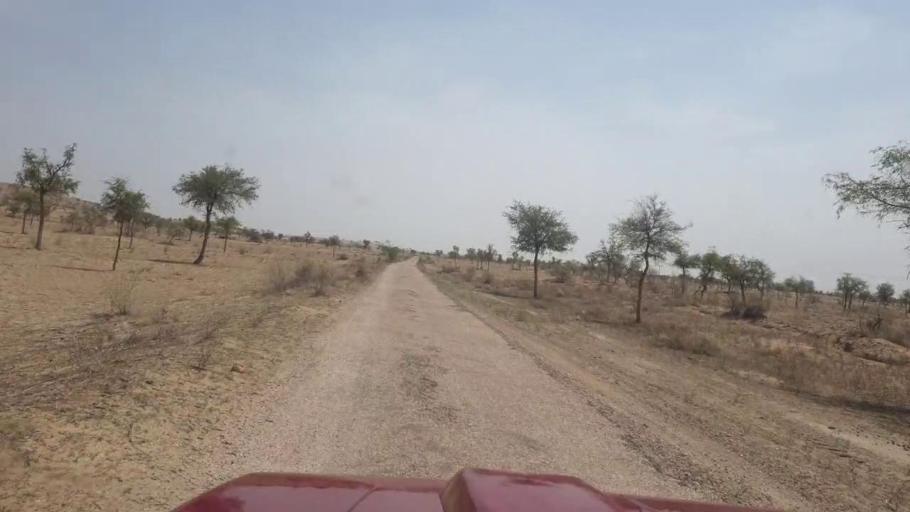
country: PK
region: Sindh
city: Islamkot
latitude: 25.1327
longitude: 70.3868
